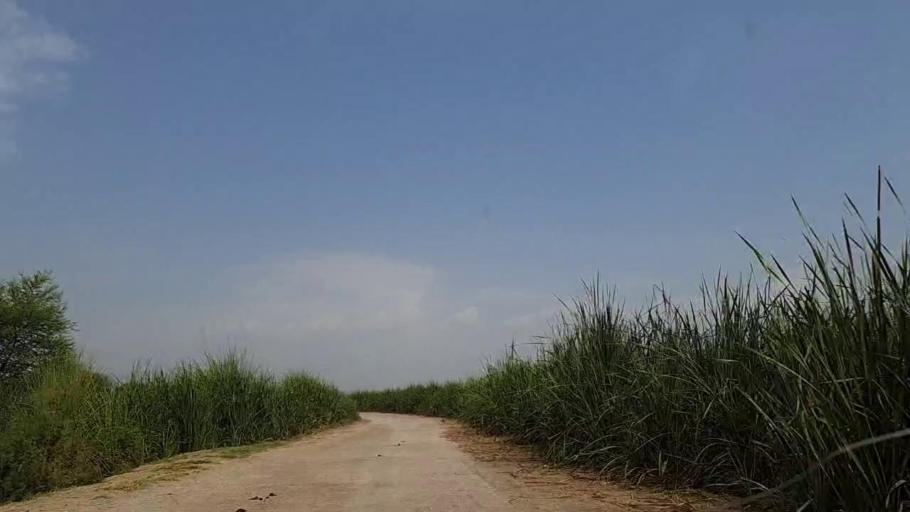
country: PK
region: Sindh
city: Khanpur
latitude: 27.8368
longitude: 69.4937
